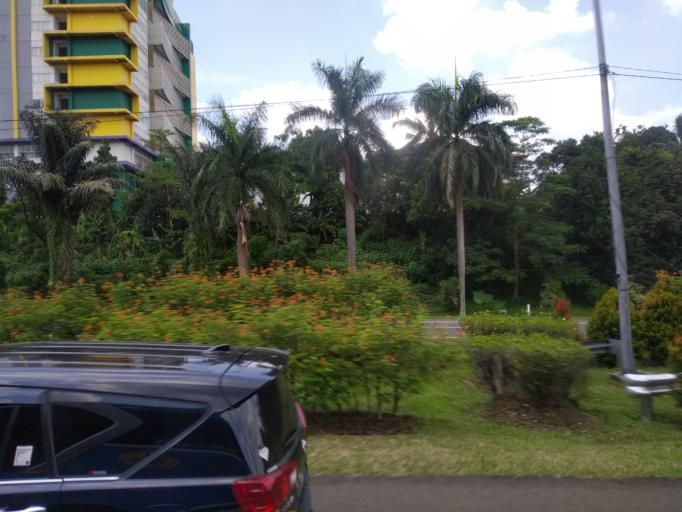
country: ID
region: West Java
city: Bogor
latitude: -6.6006
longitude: 106.8129
